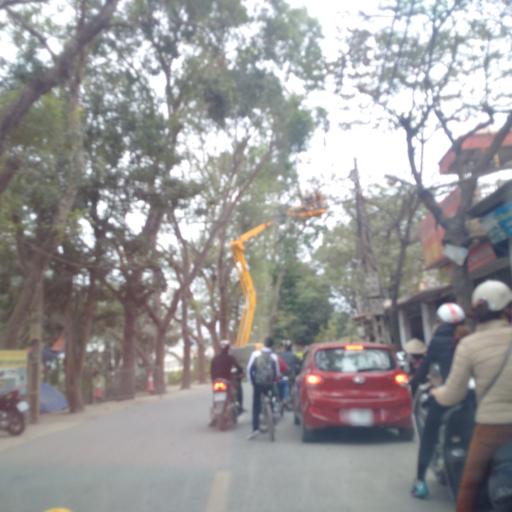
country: VN
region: Ha Noi
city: Tay Ho
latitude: 21.0836
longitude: 105.7786
